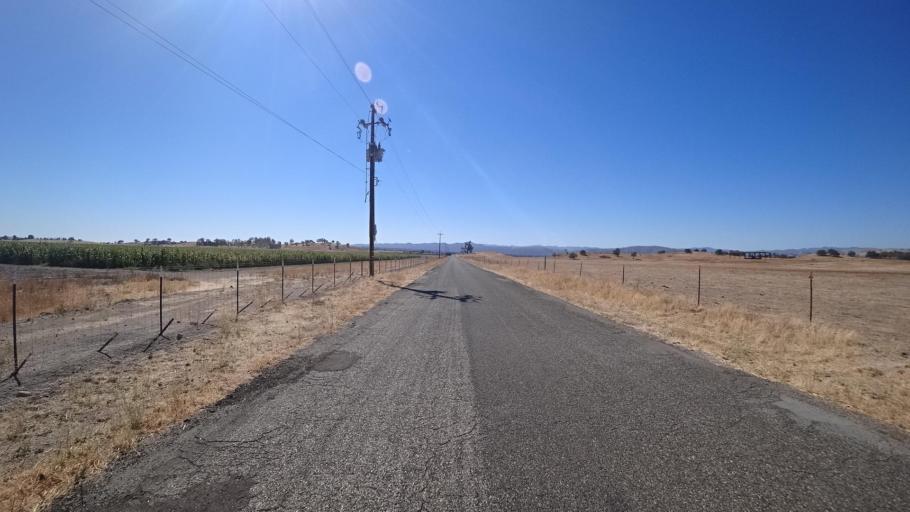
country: US
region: California
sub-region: Monterey County
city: King City
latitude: 35.9649
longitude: -121.1192
